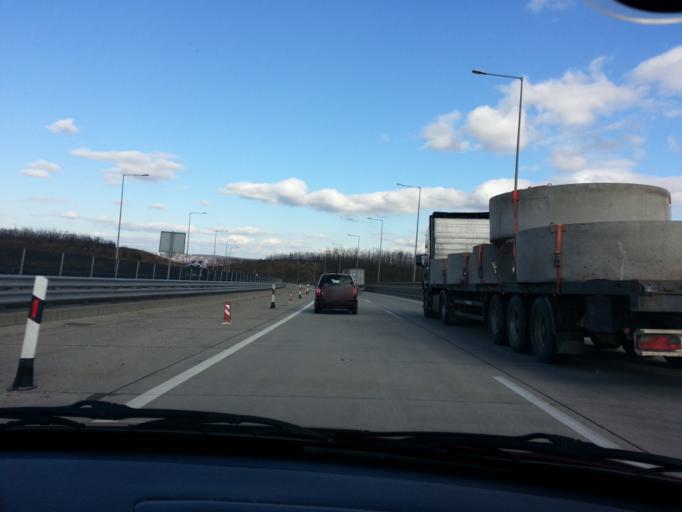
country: HU
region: Pest
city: Kerepes
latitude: 47.5668
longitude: 19.3246
